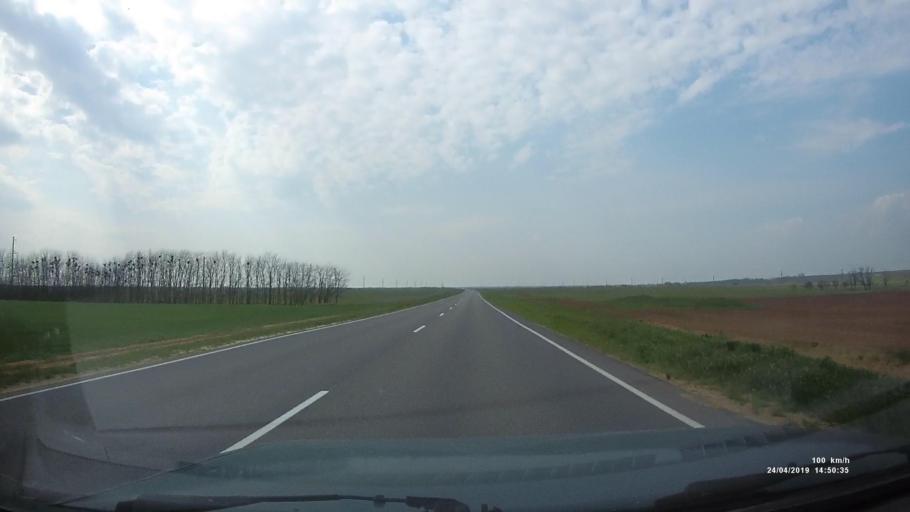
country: RU
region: Rostov
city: Remontnoye
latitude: 46.5183
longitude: 43.7168
